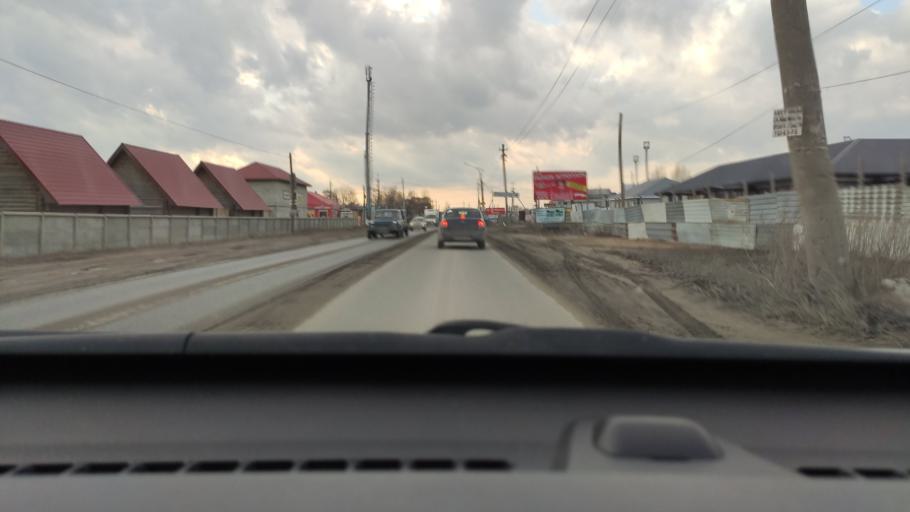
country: RU
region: Samara
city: Tol'yatti
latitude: 53.5084
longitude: 49.2483
